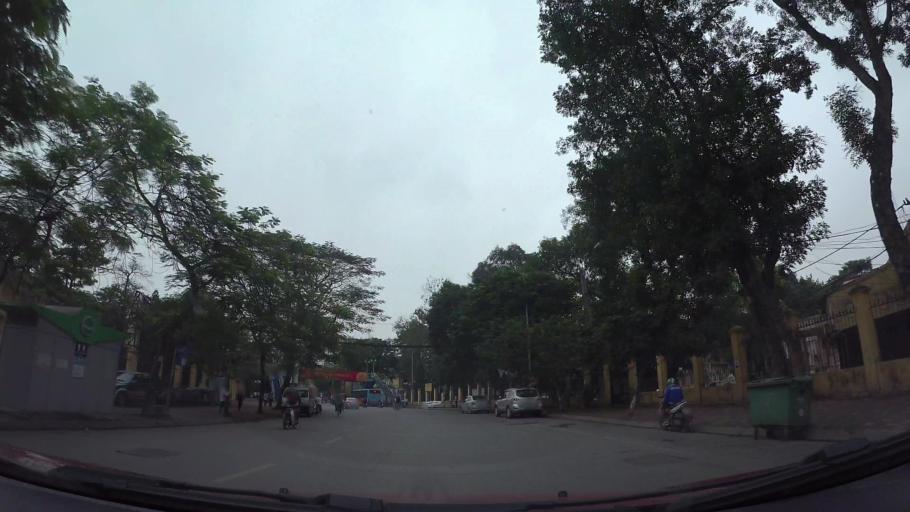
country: VN
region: Ha Noi
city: Hai BaTrung
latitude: 21.0000
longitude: 105.8452
